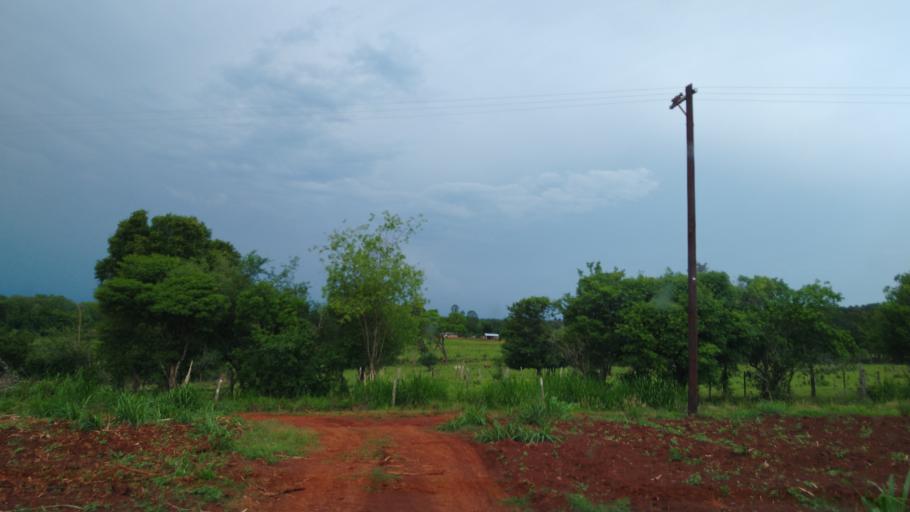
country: AR
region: Misiones
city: Capiovi
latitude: -26.9322
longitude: -55.0475
